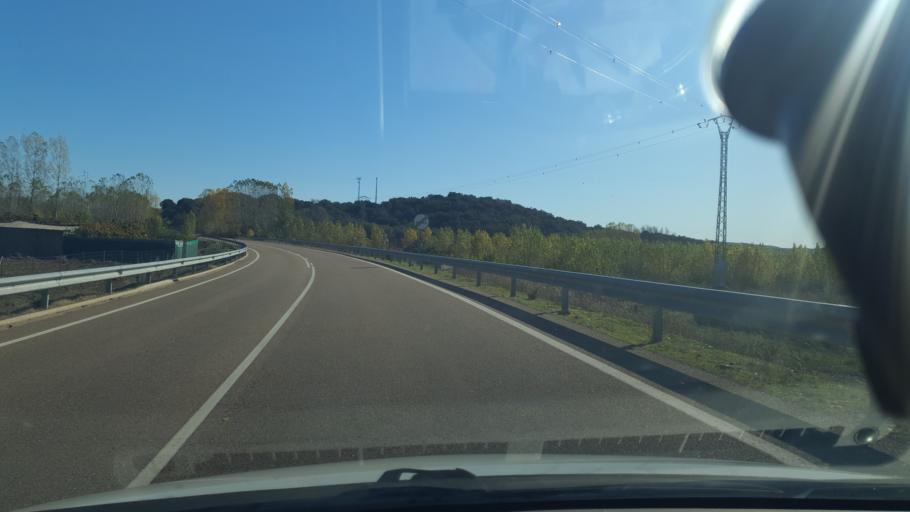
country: ES
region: Castille and Leon
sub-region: Provincia de Avila
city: Arenas de San Pedro
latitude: 40.1804
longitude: -5.0496
